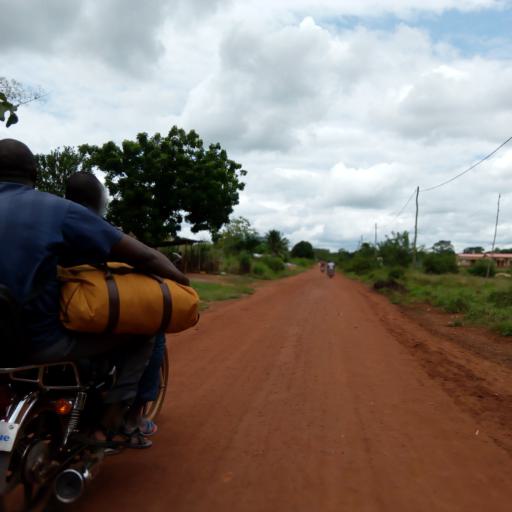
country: TG
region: Maritime
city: Tsevie
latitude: 6.3396
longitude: 1.1009
